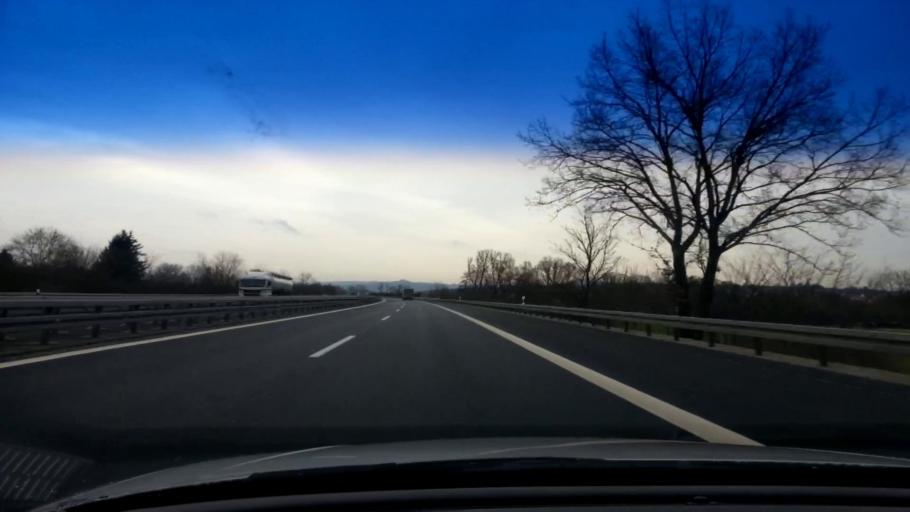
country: DE
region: Bavaria
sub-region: Upper Franconia
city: Memmelsdorf
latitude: 49.9340
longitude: 10.9420
